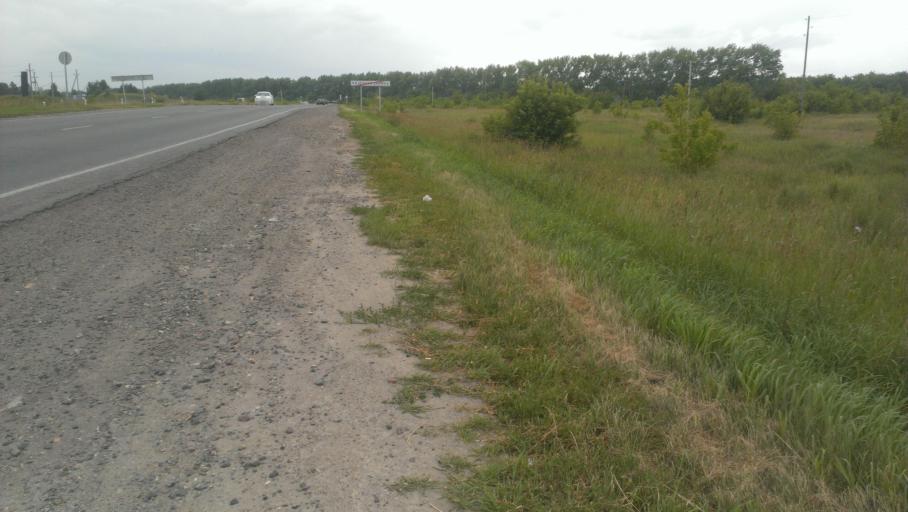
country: RU
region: Altai Krai
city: Gon'ba
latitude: 53.3897
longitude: 83.6012
